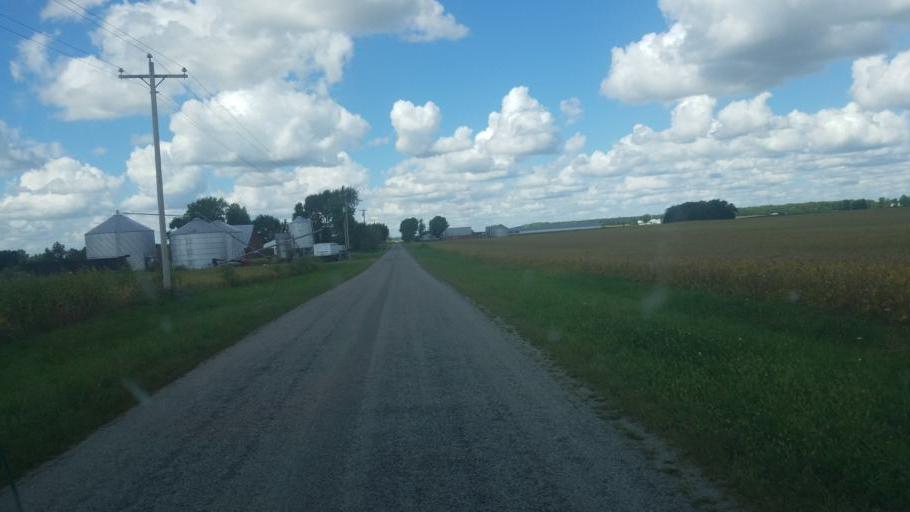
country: US
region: Ohio
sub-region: Union County
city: Richwood
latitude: 40.4490
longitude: -83.4934
